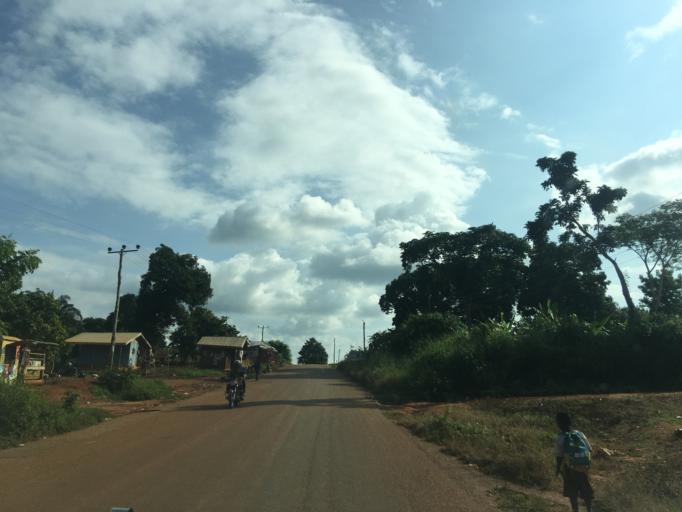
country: GH
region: Western
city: Bibiani
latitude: 6.7999
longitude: -2.5237
